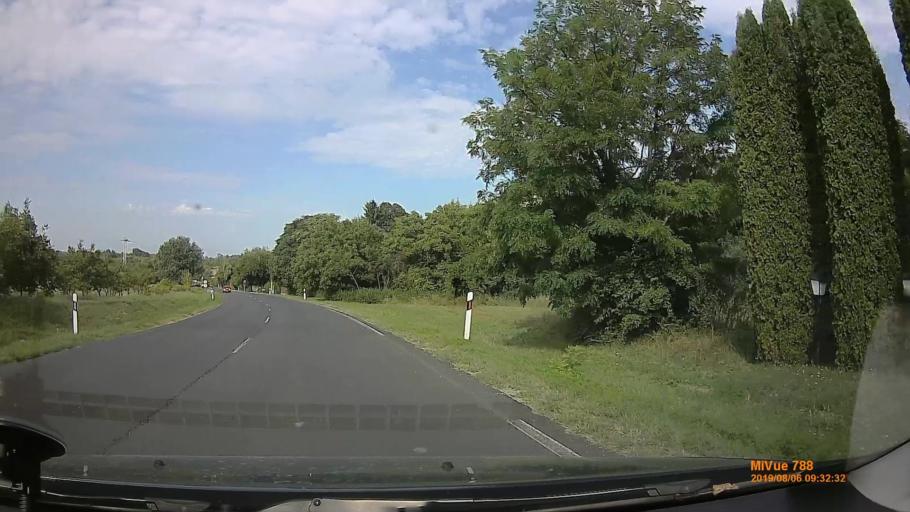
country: HU
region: Somogy
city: Balatonszarszo
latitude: 46.8257
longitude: 17.8182
